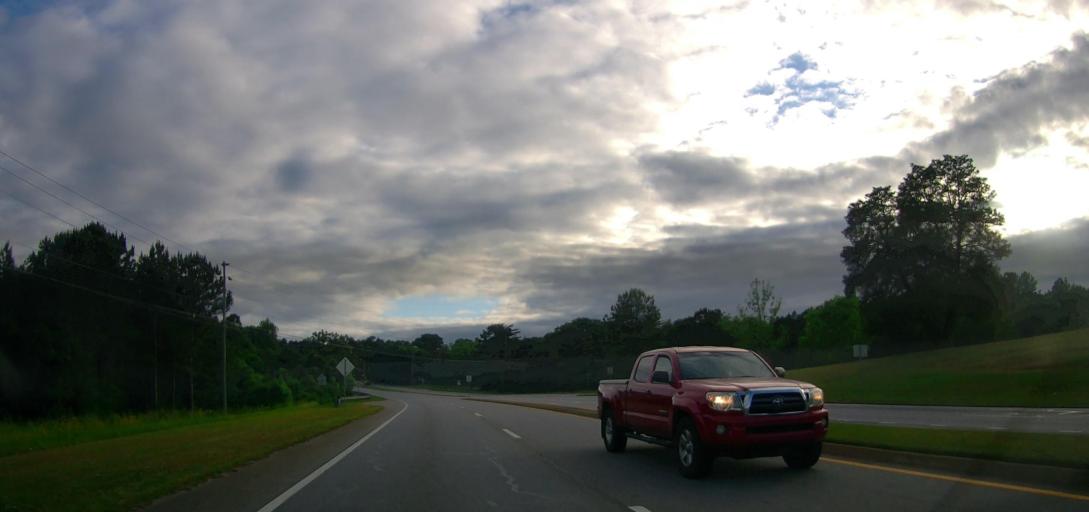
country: US
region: Georgia
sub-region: Oconee County
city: Watkinsville
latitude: 33.9023
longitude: -83.4069
